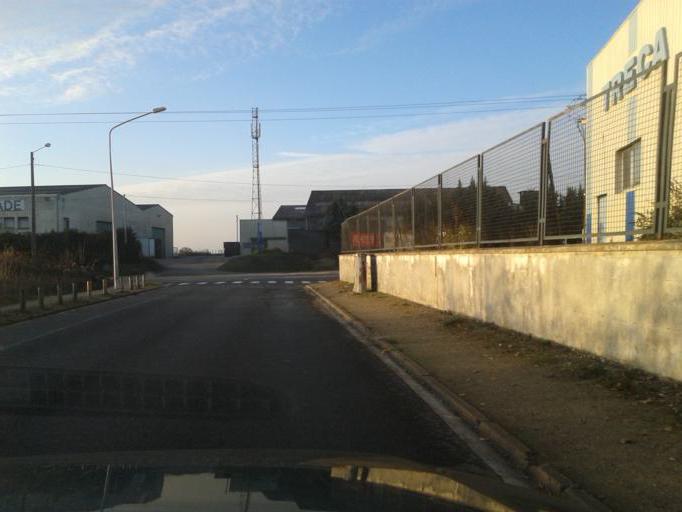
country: FR
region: Centre
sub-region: Departement du Loiret
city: Beaugency
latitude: 47.7717
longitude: 1.6196
